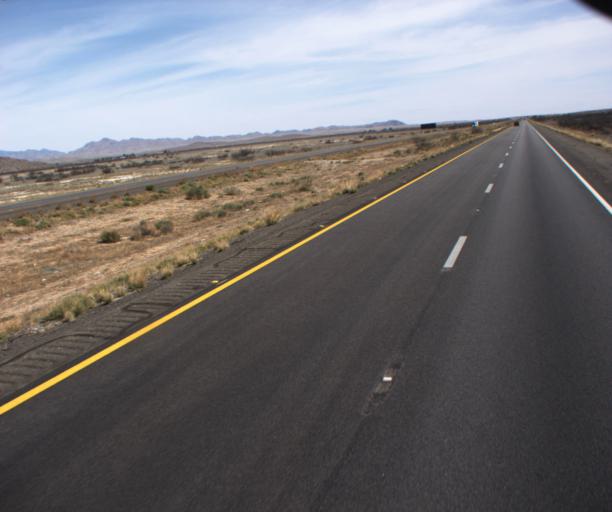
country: US
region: Arizona
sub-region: Cochise County
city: Willcox
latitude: 32.2897
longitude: -109.8187
